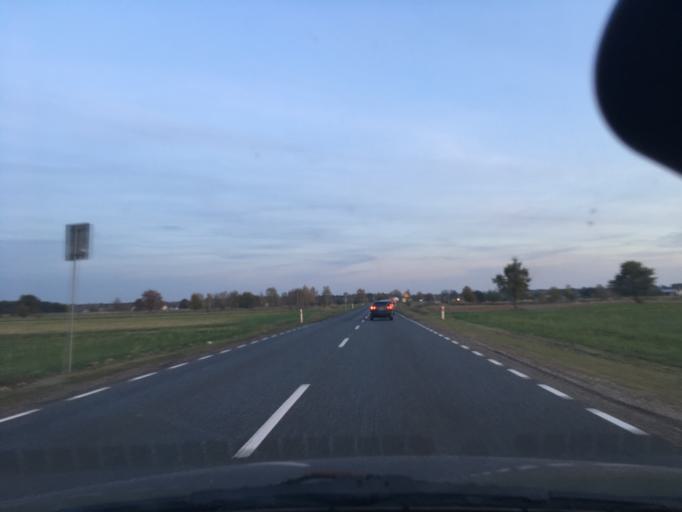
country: PL
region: Masovian Voivodeship
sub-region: Powiat plocki
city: Wyszogrod
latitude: 52.3606
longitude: 20.2018
